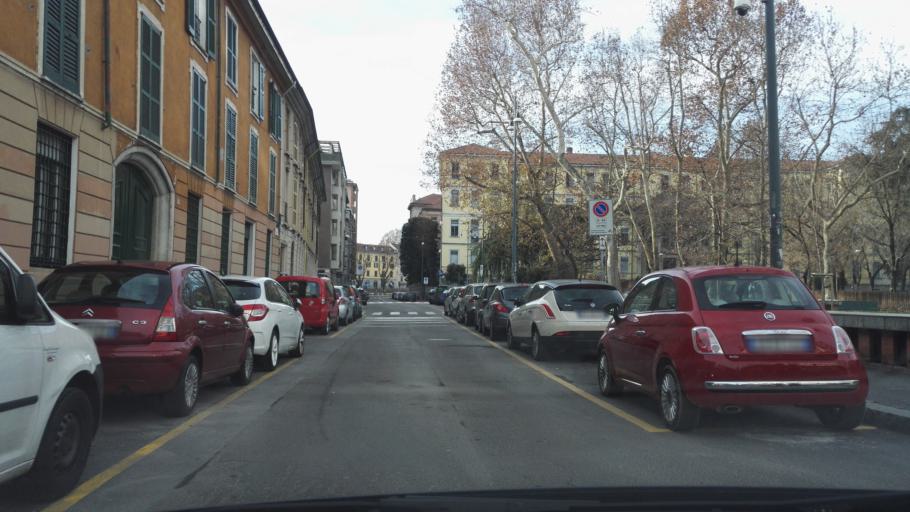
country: IT
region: Lombardy
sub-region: Citta metropolitana di Milano
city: Milano
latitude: 45.4550
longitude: 9.1785
